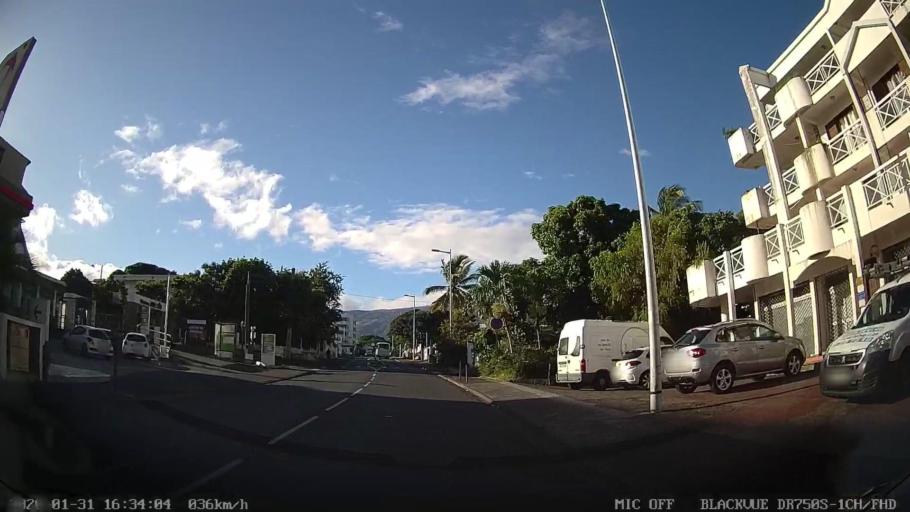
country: RE
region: Reunion
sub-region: Reunion
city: Saint-Denis
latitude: -20.8980
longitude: 55.4915
